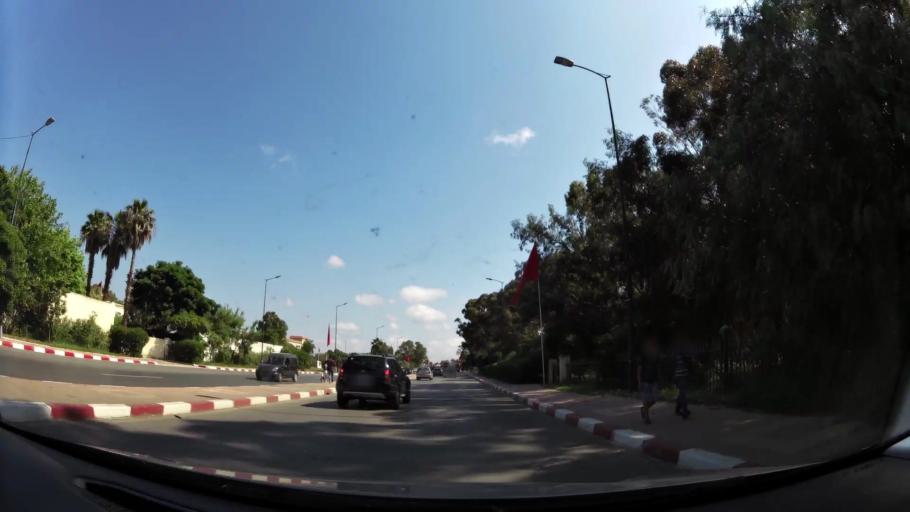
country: MA
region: Rabat-Sale-Zemmour-Zaer
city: Sale
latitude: 34.0375
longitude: -6.7755
